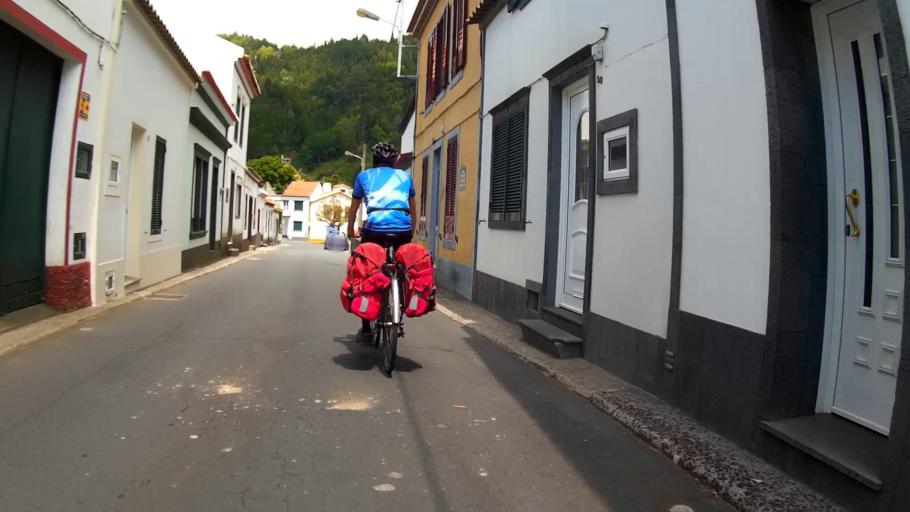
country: PT
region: Azores
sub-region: Povoacao
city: Furnas
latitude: 37.7756
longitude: -25.3122
